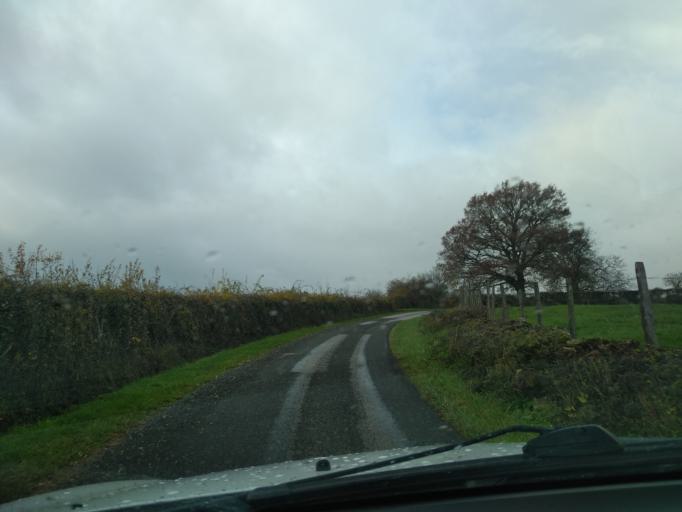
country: FR
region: Bourgogne
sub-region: Departement de Saone-et-Loire
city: Saint-Leger-sur-Dheune
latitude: 46.8426
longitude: 4.6702
